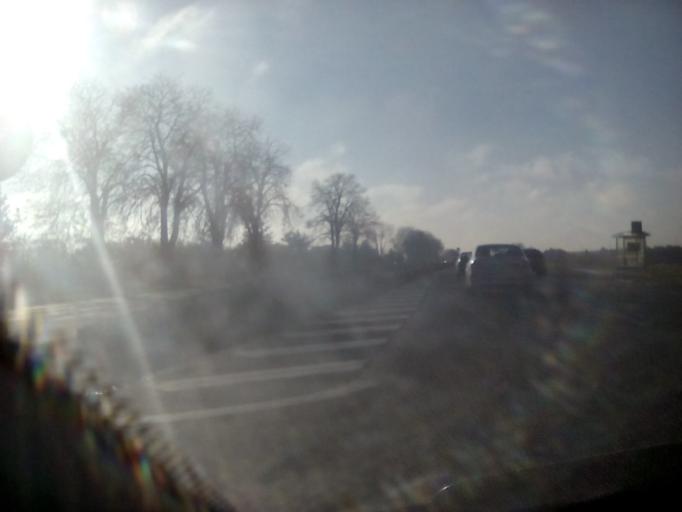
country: PL
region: Masovian Voivodeship
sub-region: Powiat piaseczynski
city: Tarczyn
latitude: 51.9408
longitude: 20.8456
